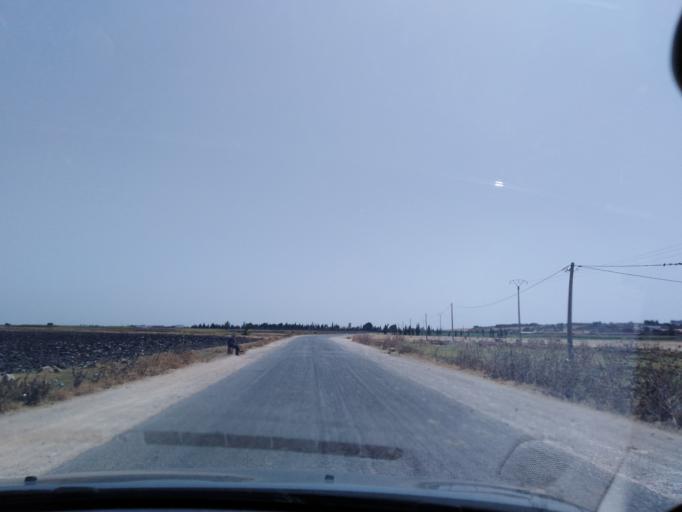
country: MA
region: Doukkala-Abda
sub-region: Safi
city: Safi
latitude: 32.4781
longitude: -8.8907
